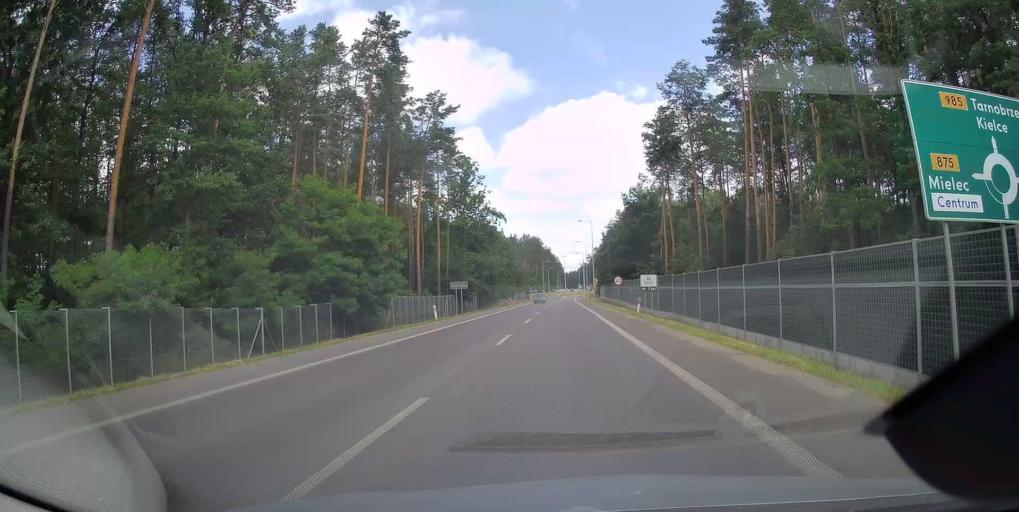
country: PL
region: Subcarpathian Voivodeship
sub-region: Powiat mielecki
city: Mielec
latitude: 50.2757
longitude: 21.4971
